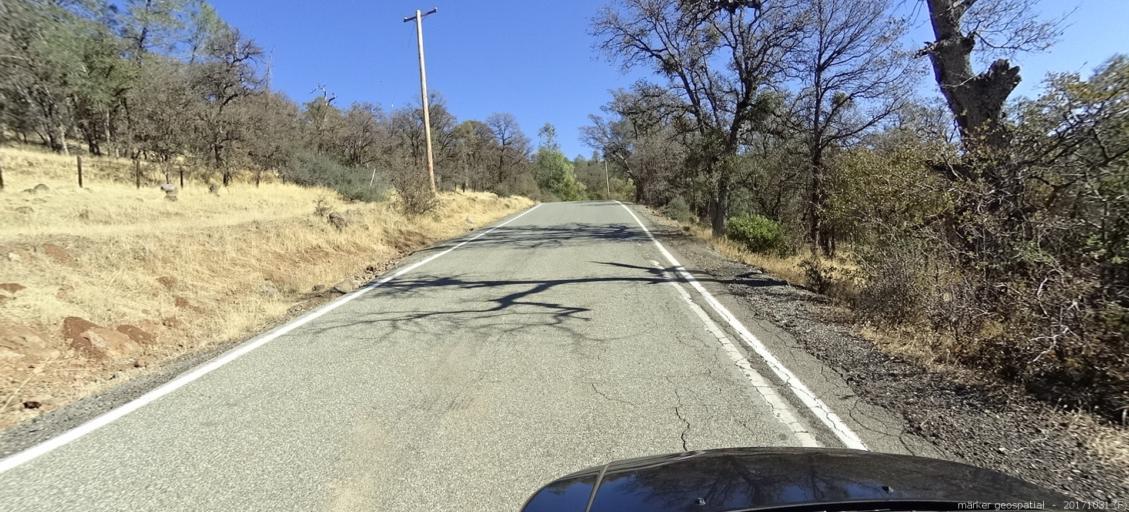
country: US
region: California
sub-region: Shasta County
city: Shingletown
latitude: 40.4653
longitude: -121.8861
